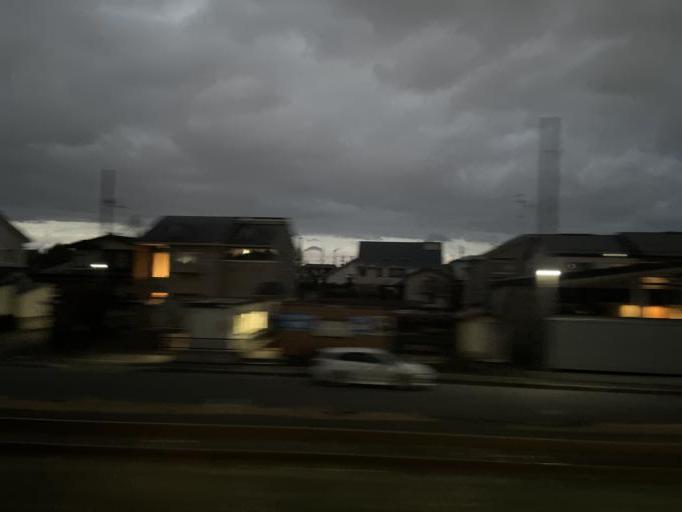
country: JP
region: Aomori
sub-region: Hachinohe Shi
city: Uchimaru
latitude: 40.5219
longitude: 141.4733
